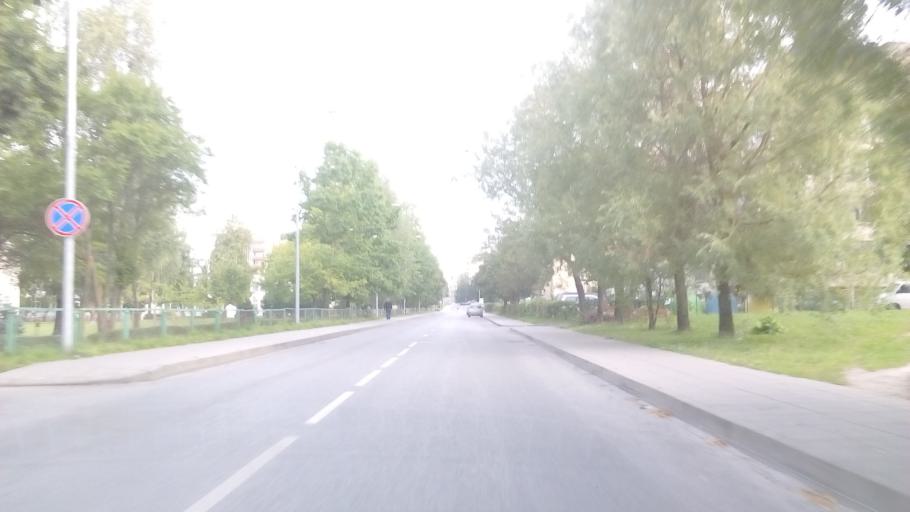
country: LT
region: Alytaus apskritis
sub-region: Alytus
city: Alytus
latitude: 54.3943
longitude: 24.0210
